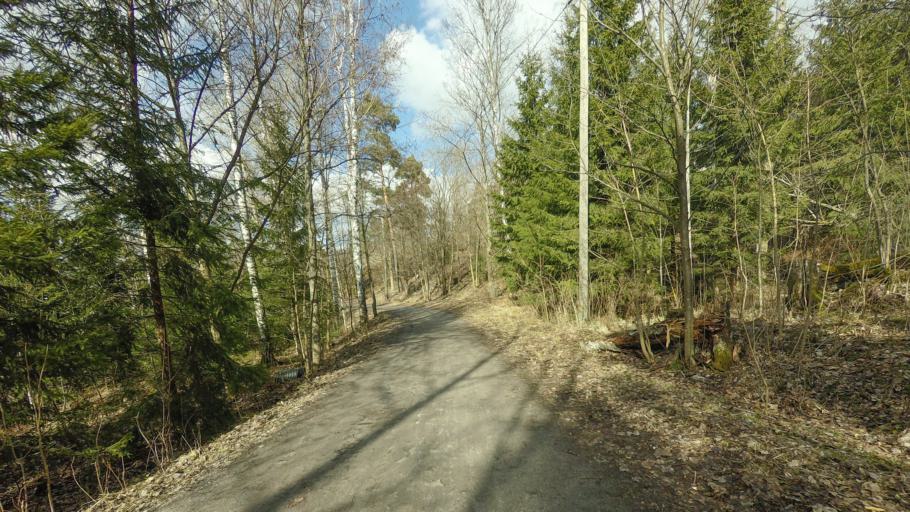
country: FI
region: Uusimaa
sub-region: Helsinki
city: Helsinki
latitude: 60.1967
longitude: 25.0251
